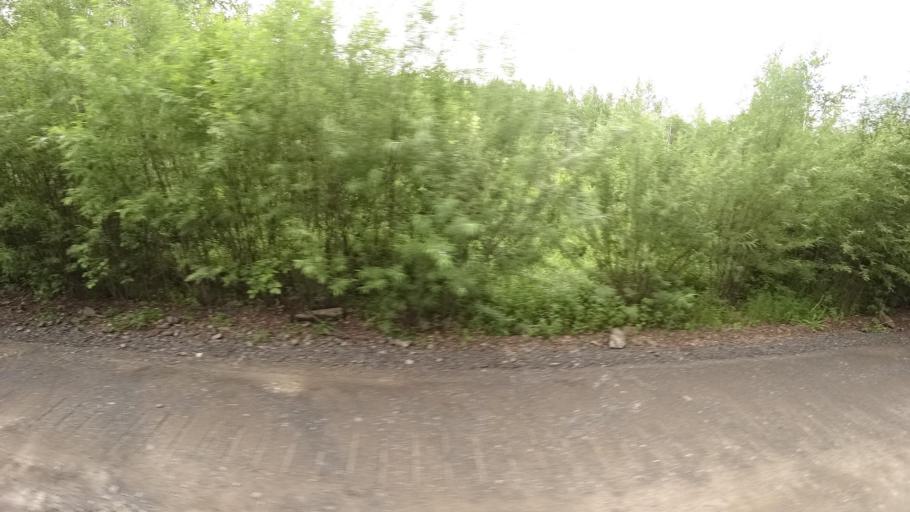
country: RU
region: Khabarovsk Krai
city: Amursk
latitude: 49.8982
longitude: 136.1306
